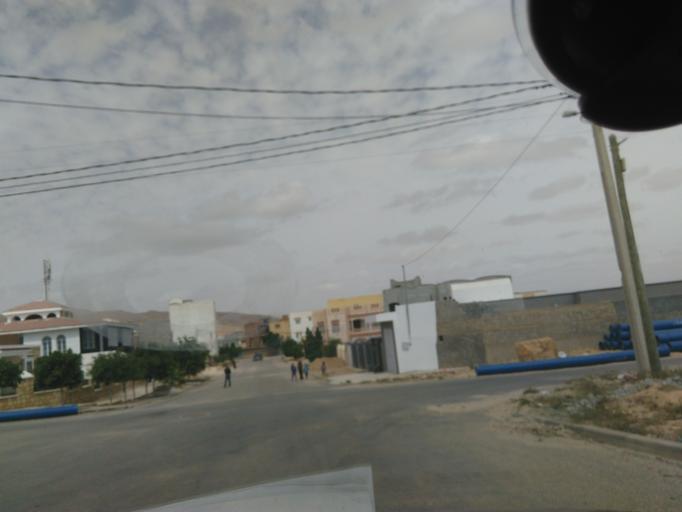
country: TN
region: Tataouine
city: Tataouine
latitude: 32.9462
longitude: 10.4674
